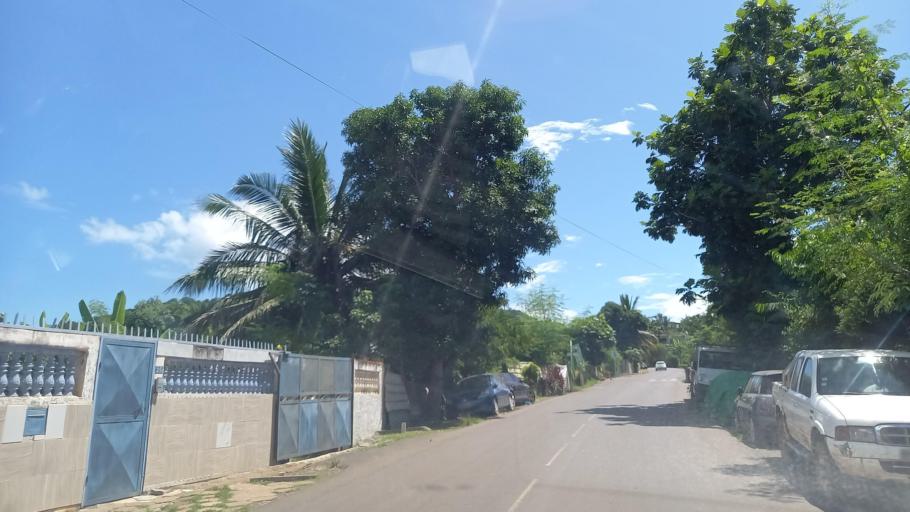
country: YT
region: Kani-Keli
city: Kani Keli
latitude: -12.9254
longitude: 45.1038
